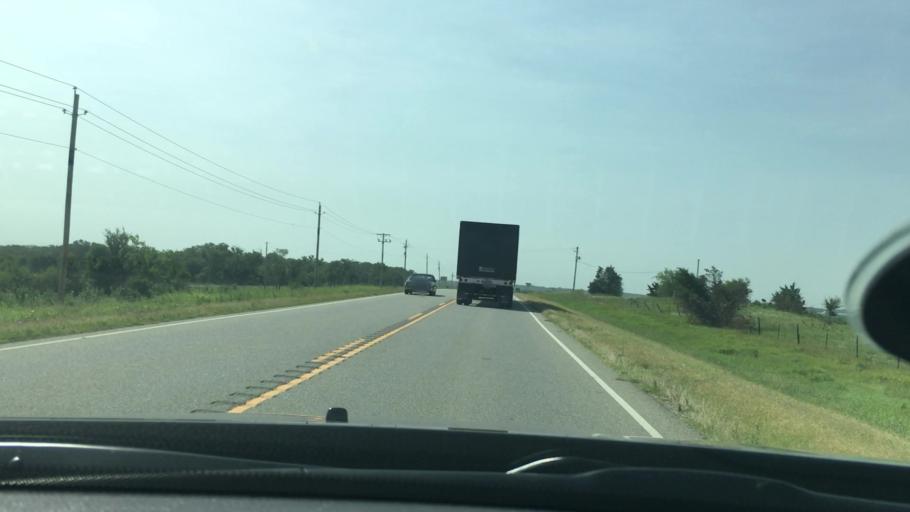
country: US
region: Oklahoma
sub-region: Atoka County
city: Atoka
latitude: 34.4203
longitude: -96.1899
